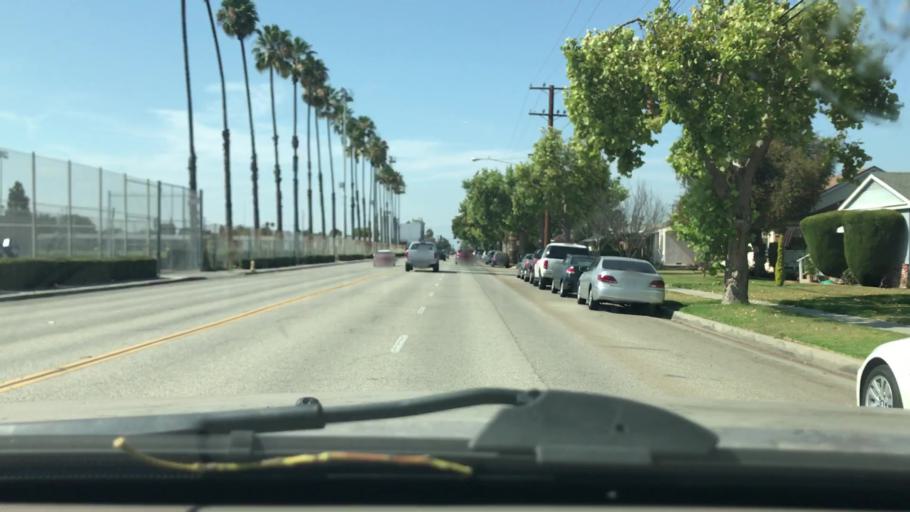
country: US
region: California
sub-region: Orange County
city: Rossmoor
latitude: 33.8063
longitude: -118.1079
